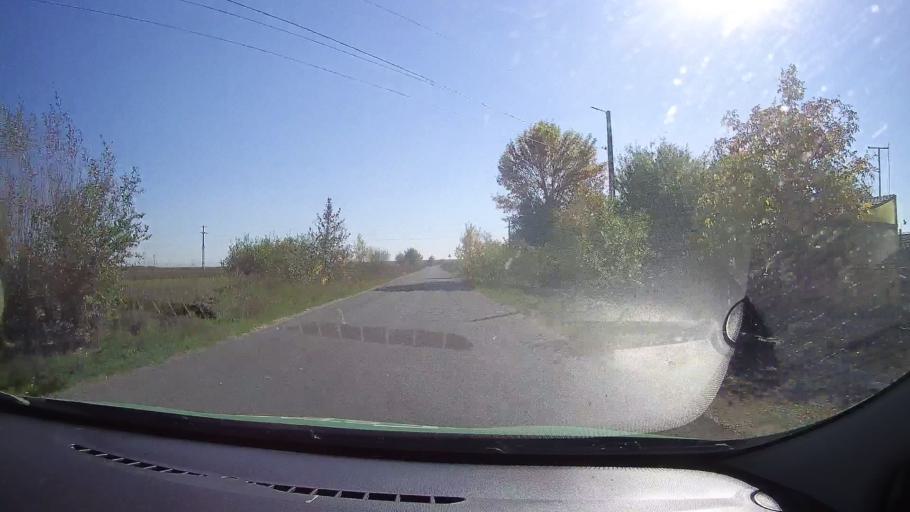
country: RO
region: Satu Mare
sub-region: Comuna Doba
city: Doba
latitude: 47.7401
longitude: 22.7170
